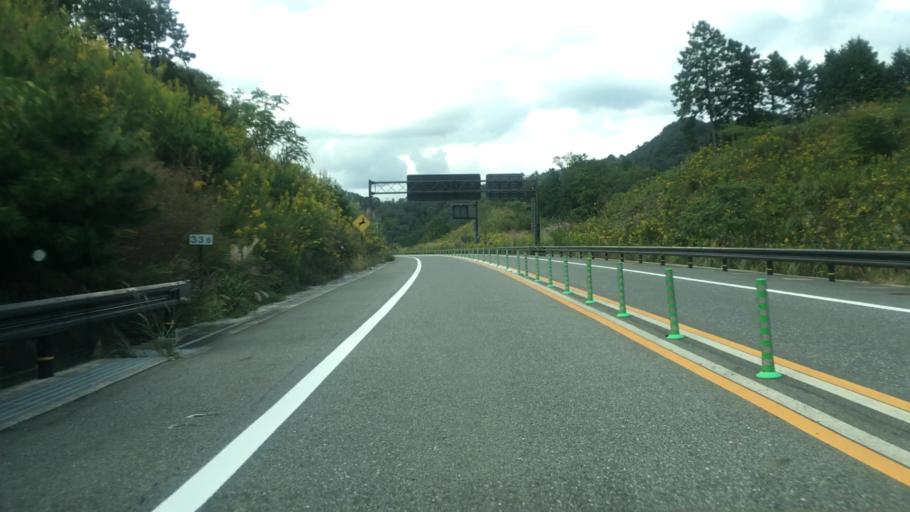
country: JP
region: Hyogo
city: Toyooka
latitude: 35.3267
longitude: 134.8380
